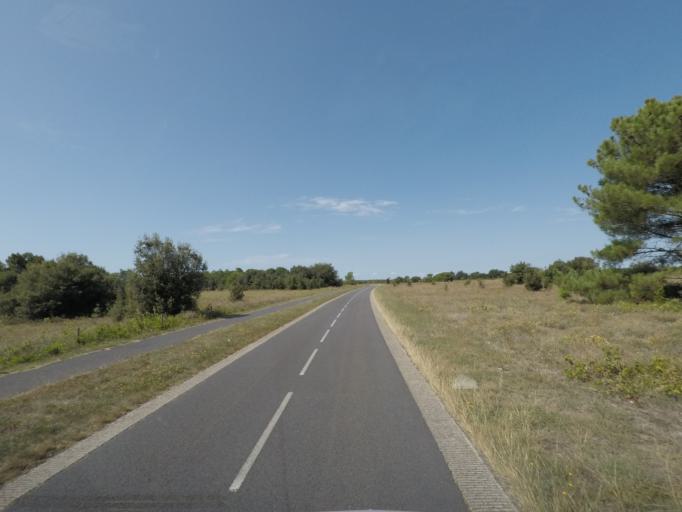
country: FR
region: Poitou-Charentes
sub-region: Departement de la Charente-Maritime
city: Sainte-Marie-de-Re
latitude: 46.1577
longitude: -1.3166
